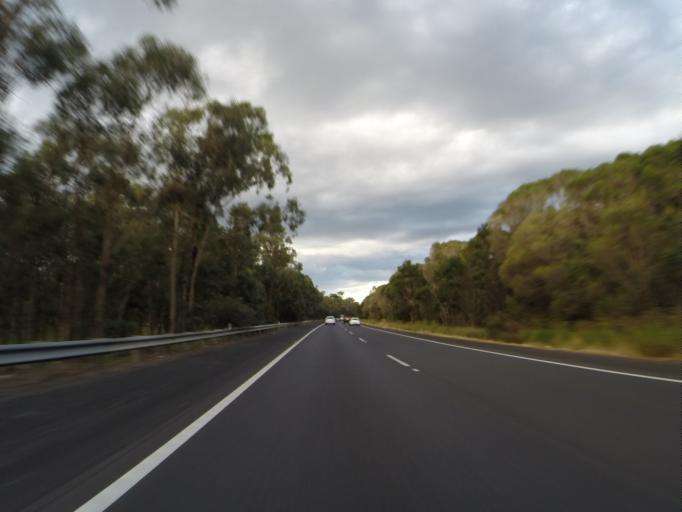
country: AU
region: New South Wales
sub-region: Wollondilly
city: Buxton
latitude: -34.3025
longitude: 150.6082
